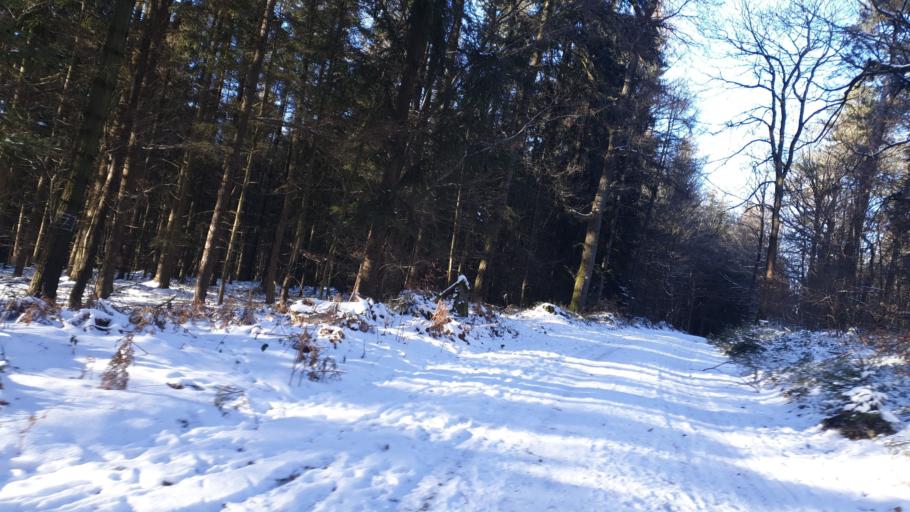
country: DE
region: Hesse
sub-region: Regierungsbezirk Darmstadt
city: Beerfelden
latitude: 49.5457
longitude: 8.9915
